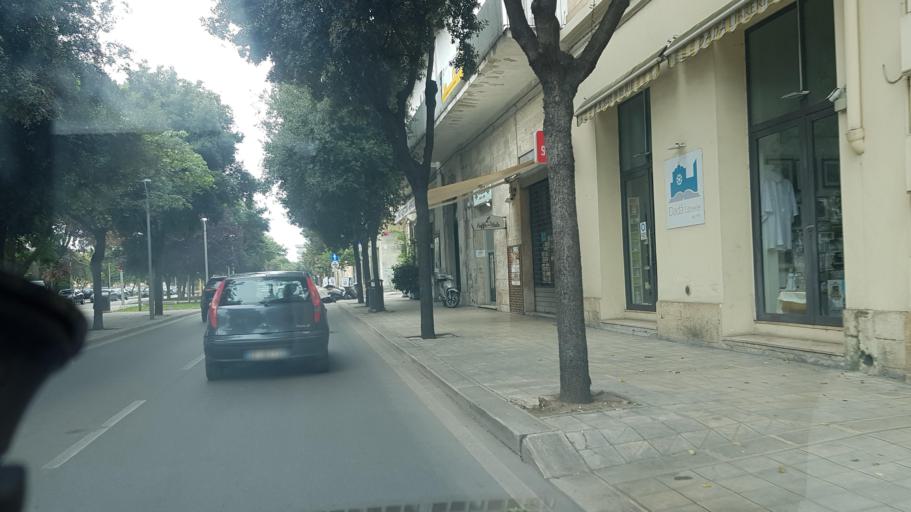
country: IT
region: Apulia
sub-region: Provincia di Lecce
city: Lecce
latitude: 40.3541
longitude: 18.1654
